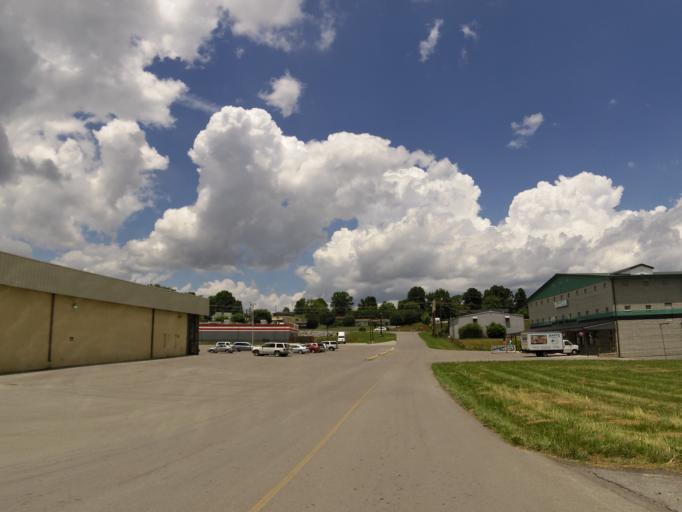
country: US
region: Tennessee
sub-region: Claiborne County
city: New Tazewell
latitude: 36.4446
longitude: -83.5913
